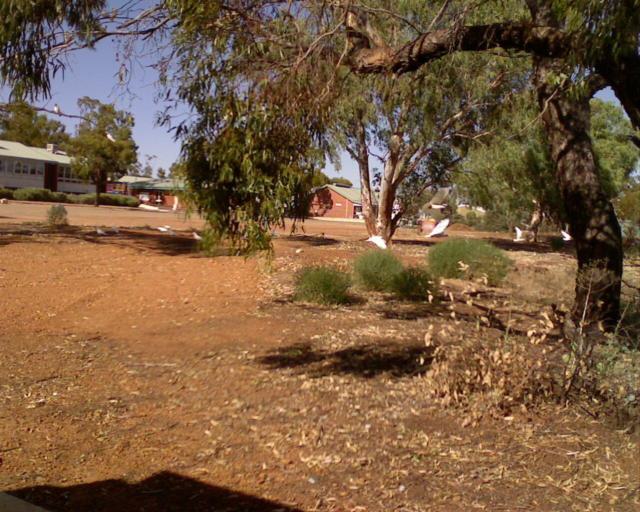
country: AU
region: Western Australia
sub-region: Wongan-Ballidu
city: Wongan Hills
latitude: -30.2697
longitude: 116.6625
